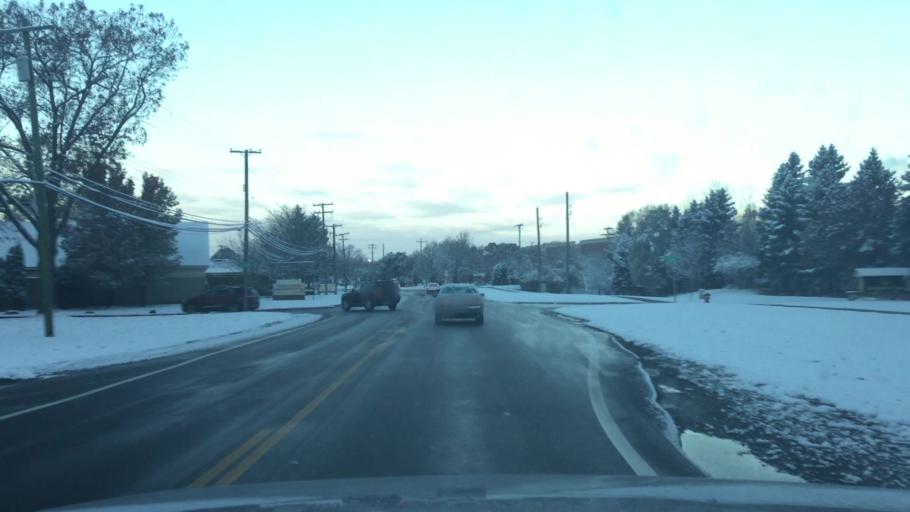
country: US
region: Michigan
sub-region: Oakland County
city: Wolverine Lake
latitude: 42.5922
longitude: -83.4414
